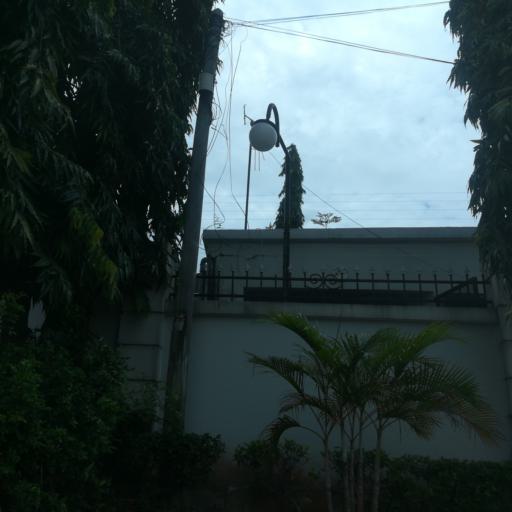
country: NG
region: Lagos
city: Ikoyi
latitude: 6.4462
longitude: 3.4667
